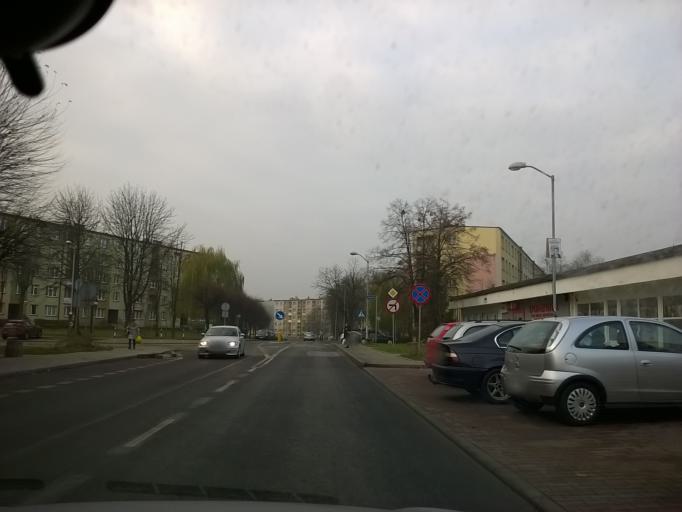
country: PL
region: Silesian Voivodeship
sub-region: Ruda Slaska
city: Ruda Slaska
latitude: 50.2432
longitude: 18.8287
